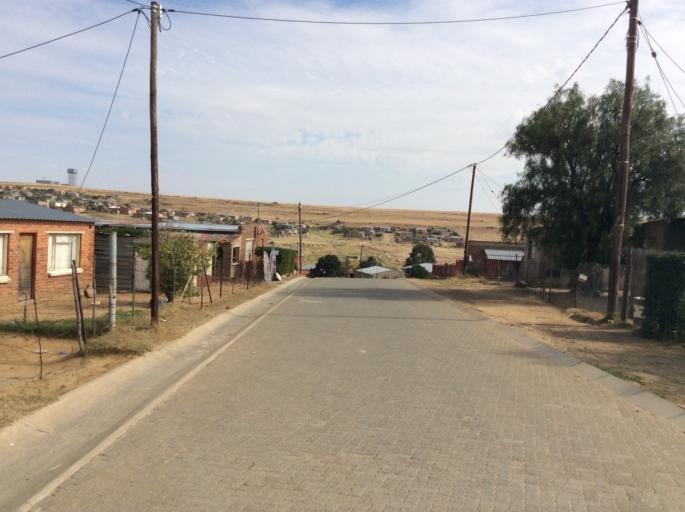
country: ZA
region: Orange Free State
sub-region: Xhariep District Municipality
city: Dewetsdorp
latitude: -29.5893
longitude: 26.6809
